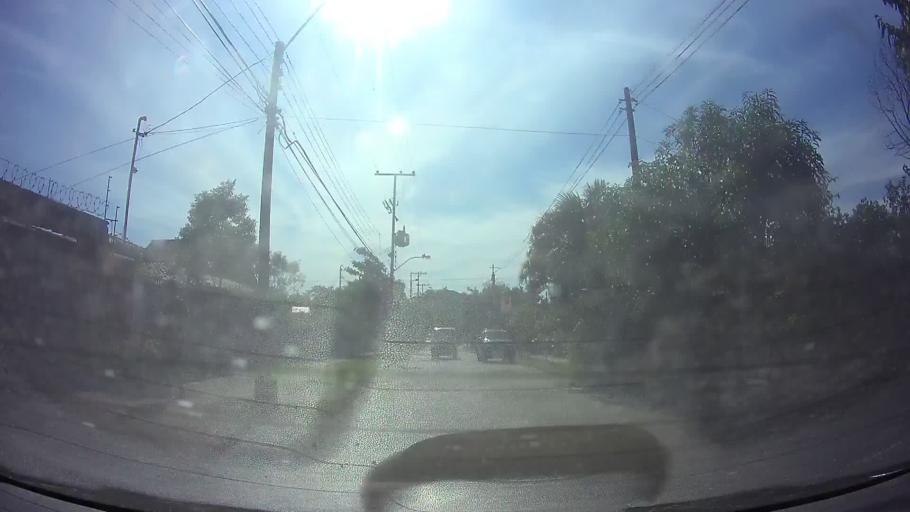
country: PY
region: Central
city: Fernando de la Mora
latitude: -25.2830
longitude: -57.5448
